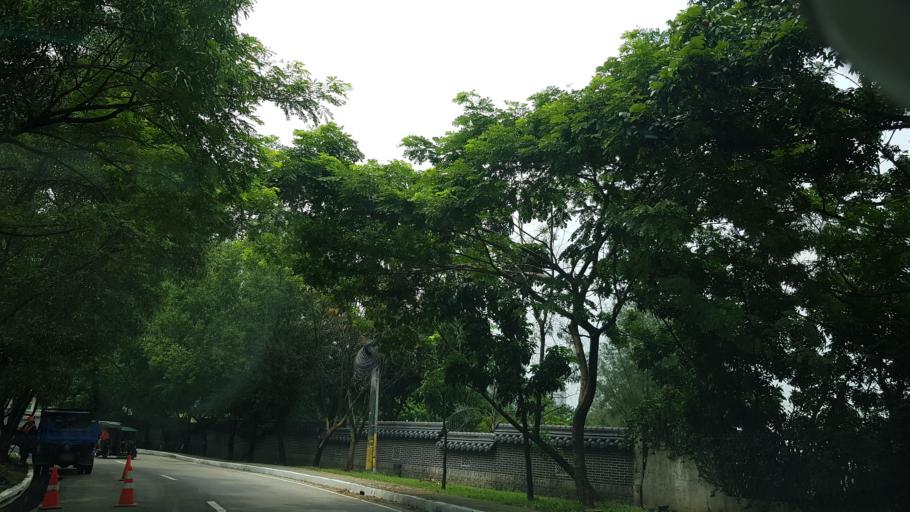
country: PH
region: Metro Manila
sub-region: Makati City
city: Makati City
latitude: 14.5243
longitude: 121.0464
